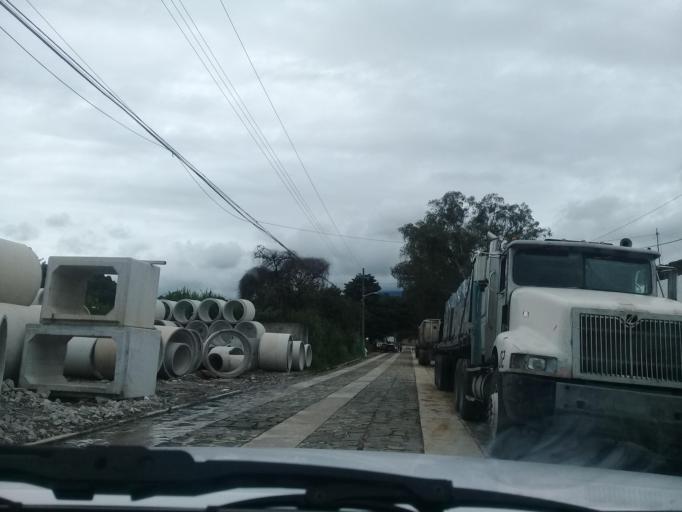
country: MX
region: Veracruz
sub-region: Rafael Lucio
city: Piletas
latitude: 19.5902
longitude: -96.9713
